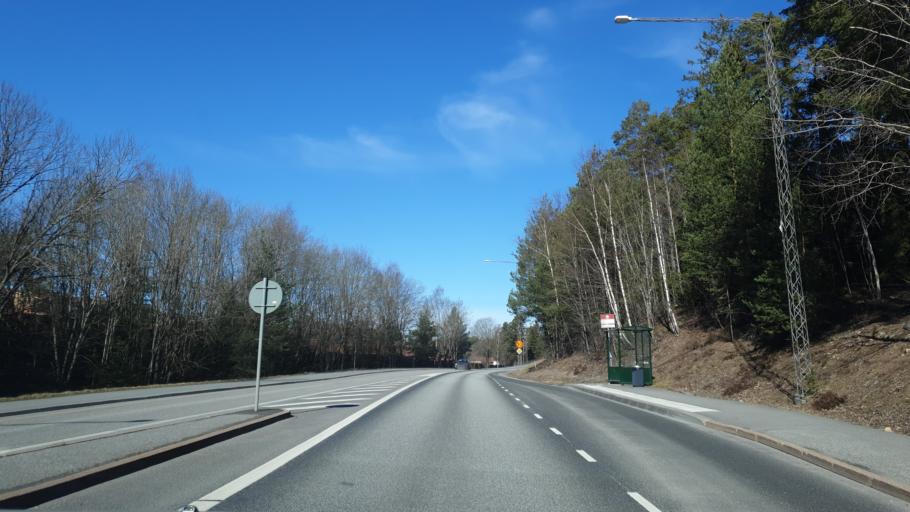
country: SE
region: Stockholm
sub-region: Jarfalla Kommun
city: Jakobsberg
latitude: 59.4404
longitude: 17.8400
